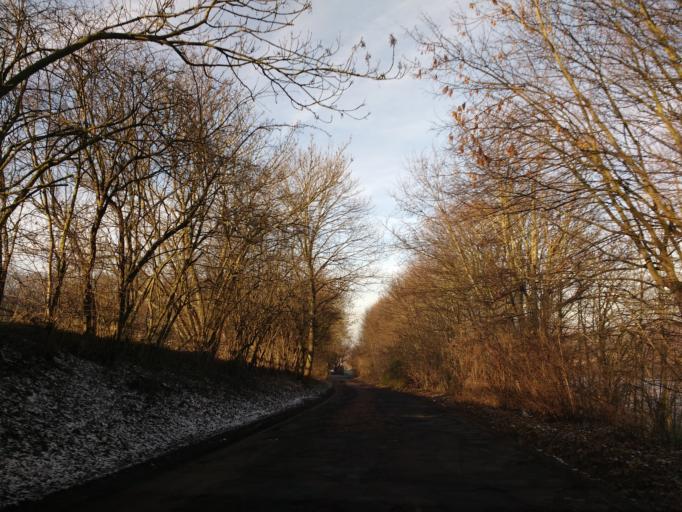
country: DE
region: Saxony-Anhalt
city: Gutenberg
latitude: 51.5308
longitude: 11.9829
